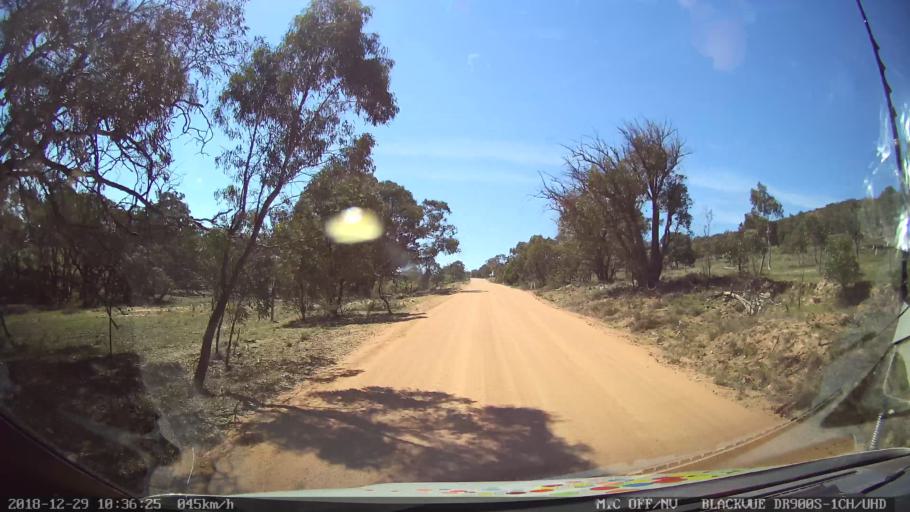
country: AU
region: New South Wales
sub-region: Yass Valley
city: Gundaroo
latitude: -34.9938
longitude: 149.4908
